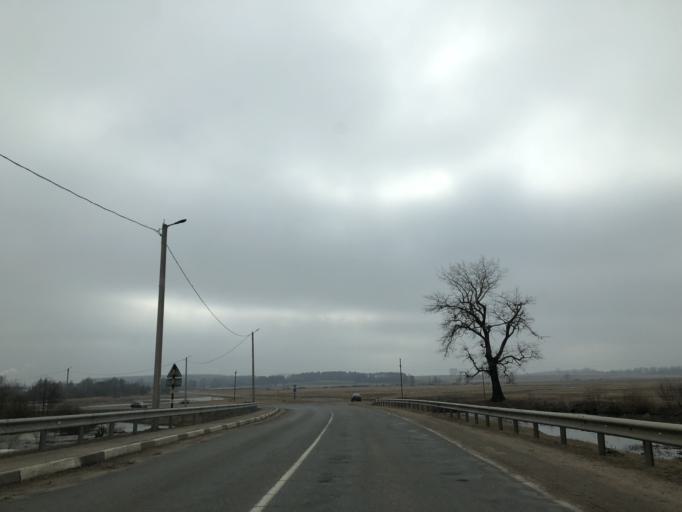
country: BY
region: Minsk
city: Novy Svyerzhan'
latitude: 53.4692
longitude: 26.7275
